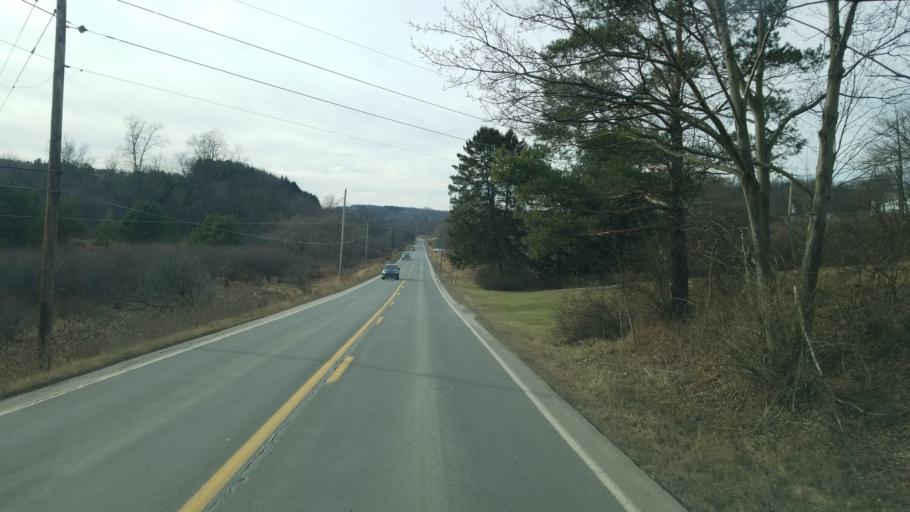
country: US
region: Pennsylvania
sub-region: Jefferson County
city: Punxsutawney
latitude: 40.9054
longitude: -79.0230
